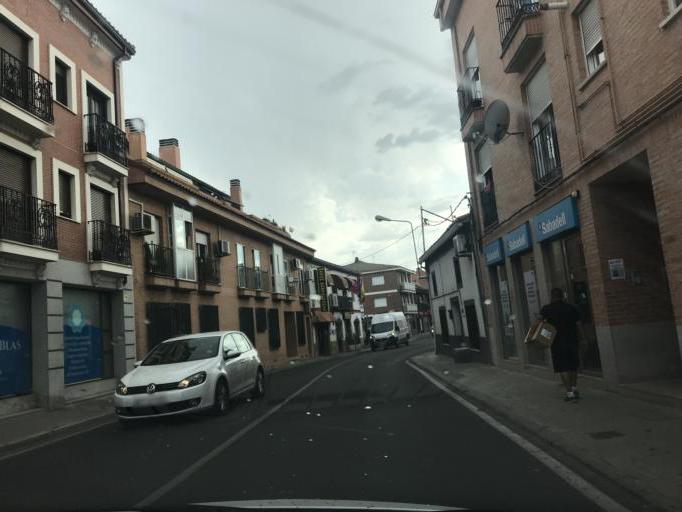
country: ES
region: Madrid
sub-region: Provincia de Madrid
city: Paracuellos de Jarama
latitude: 40.5047
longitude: -3.5300
